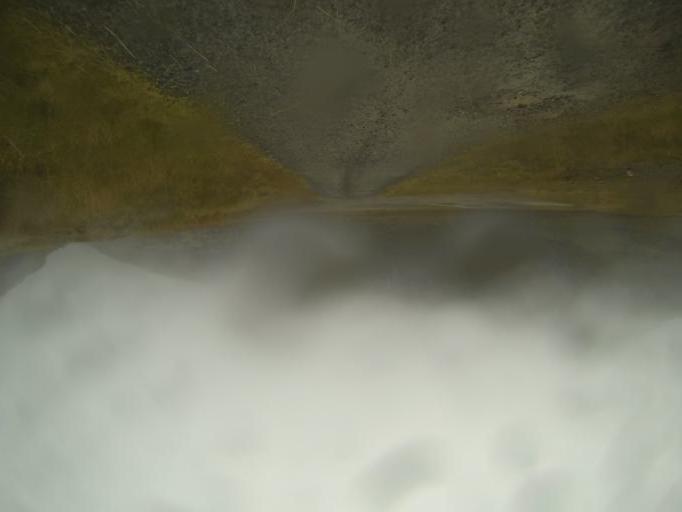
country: NO
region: Vest-Agder
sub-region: Sirdal
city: Tonstad
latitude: 58.8933
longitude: 6.6660
